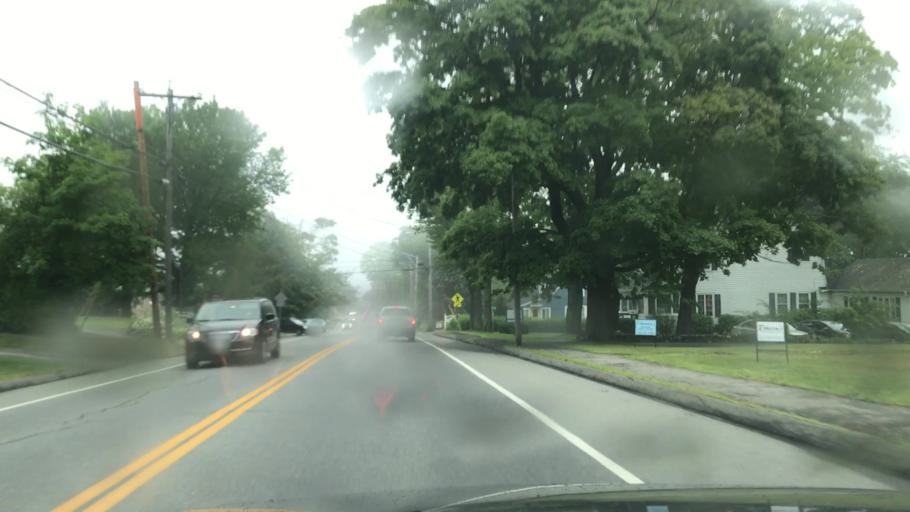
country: US
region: Maine
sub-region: Knox County
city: Camden
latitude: 44.2040
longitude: -69.0727
